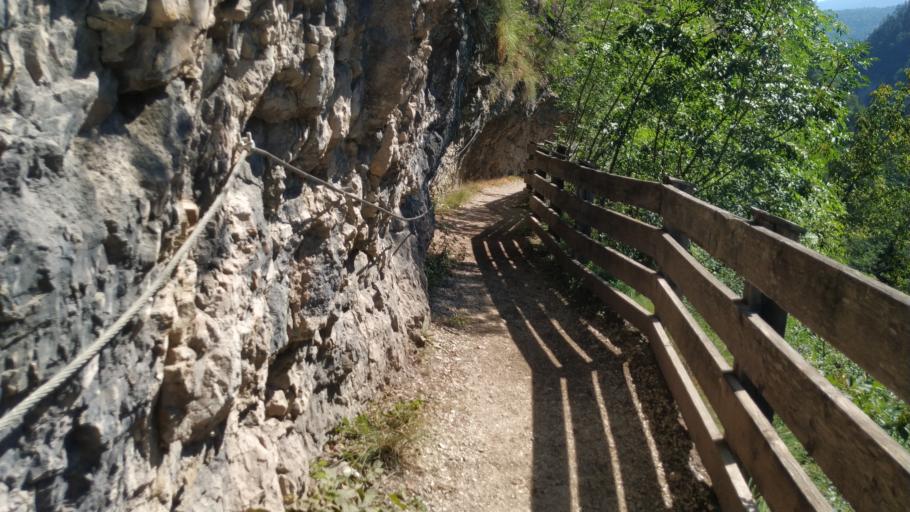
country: IT
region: Trentino-Alto Adige
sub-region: Provincia di Trento
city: Sanzeno
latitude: 46.3690
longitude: 11.0864
